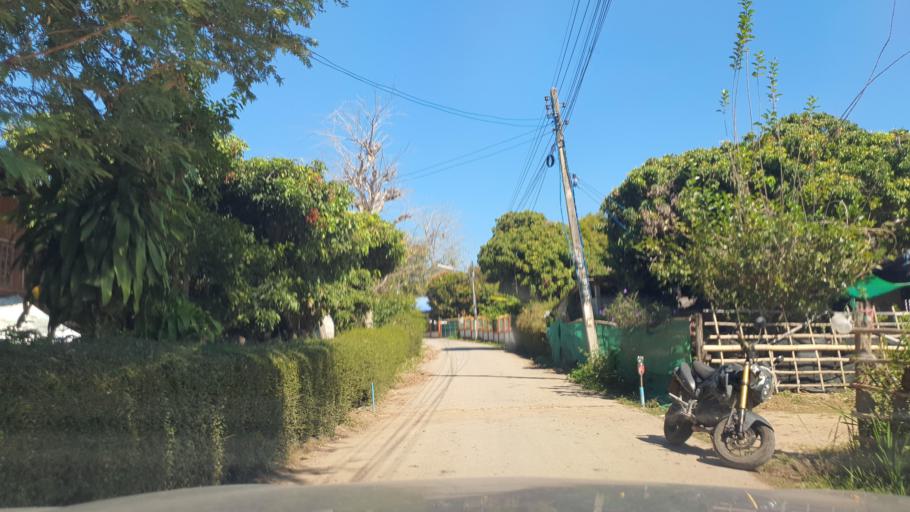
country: TH
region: Chiang Mai
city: Mae Wang
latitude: 18.6779
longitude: 98.8183
